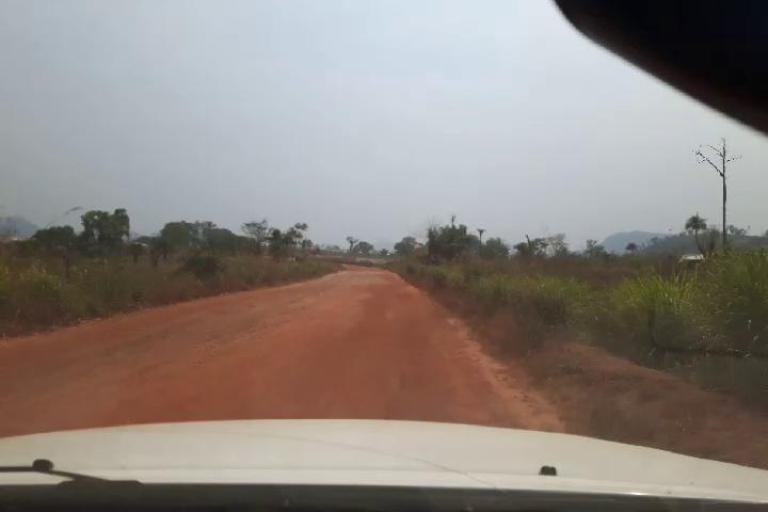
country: SL
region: Northern Province
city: Bumbuna
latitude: 9.0062
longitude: -11.7733
